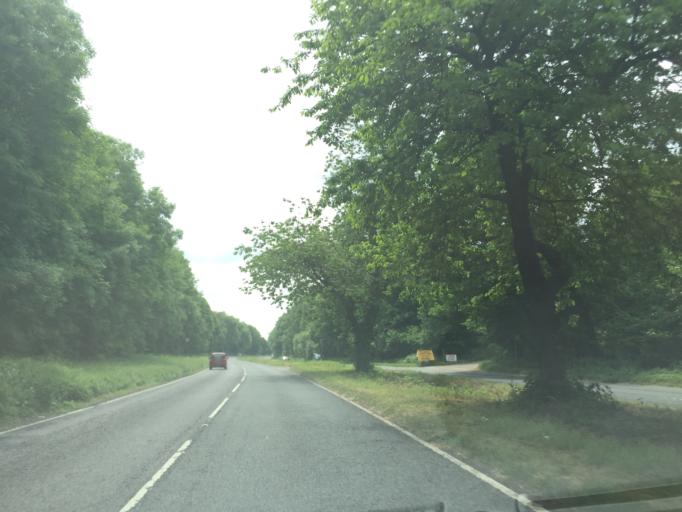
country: GB
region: England
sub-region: Hampshire
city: Four Marks
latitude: 51.1248
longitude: -1.0165
